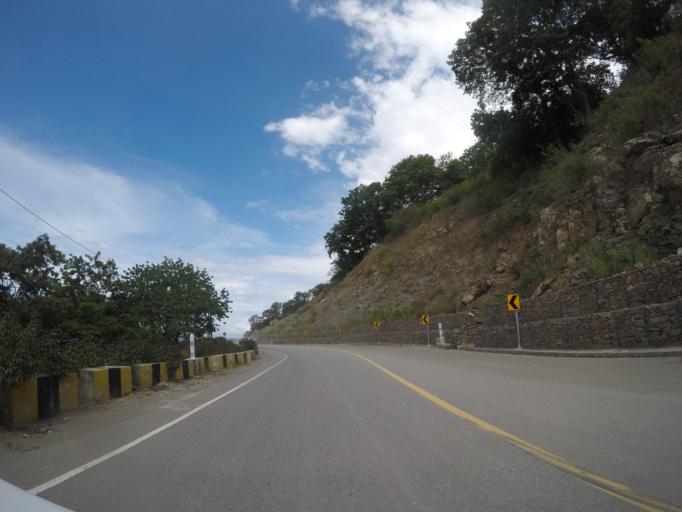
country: TL
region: Liquica
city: Maubara
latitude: -8.6397
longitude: 125.1302
